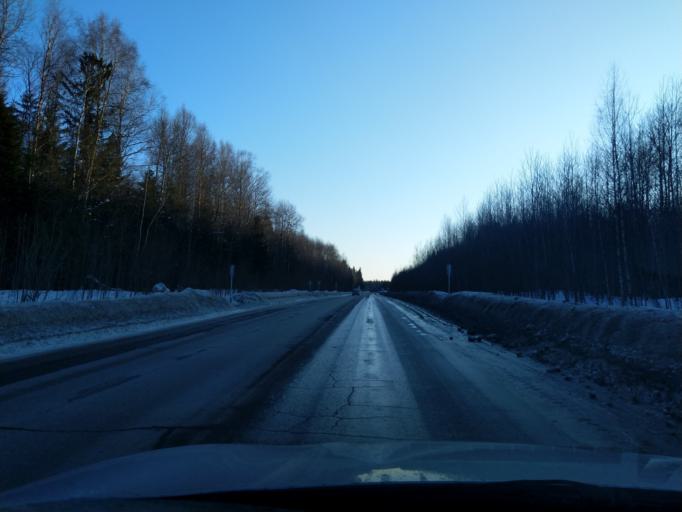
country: RU
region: Perm
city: Dobryanka
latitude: 58.4513
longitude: 56.5457
